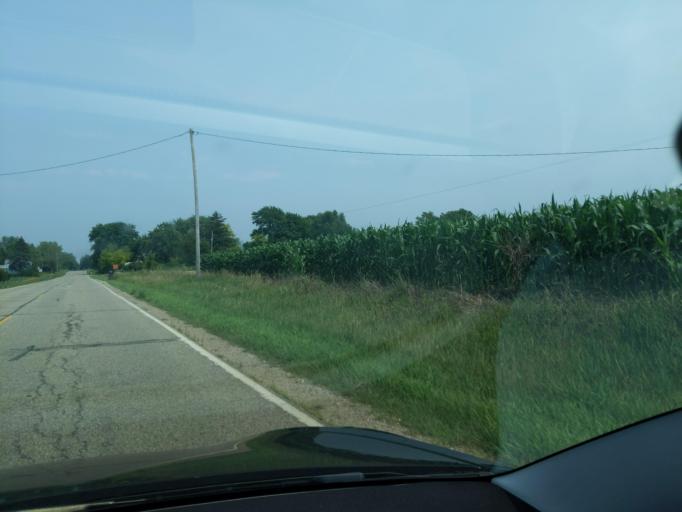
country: US
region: Michigan
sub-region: Clinton County
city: Saint Johns
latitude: 42.9290
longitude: -84.5778
